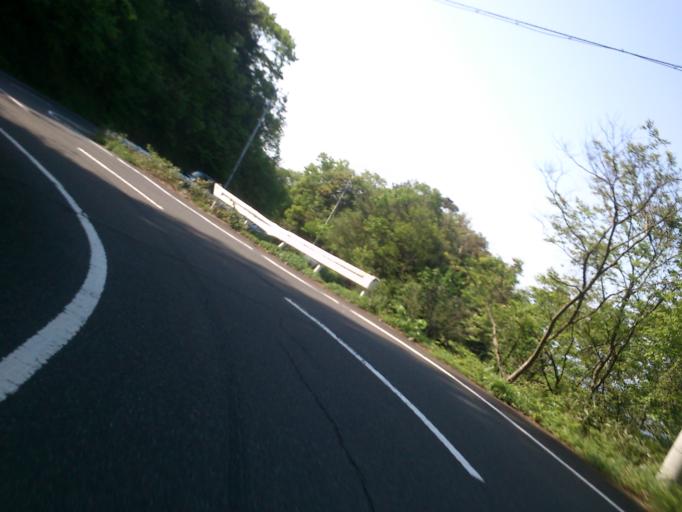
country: JP
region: Kyoto
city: Miyazu
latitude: 35.7289
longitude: 135.1849
